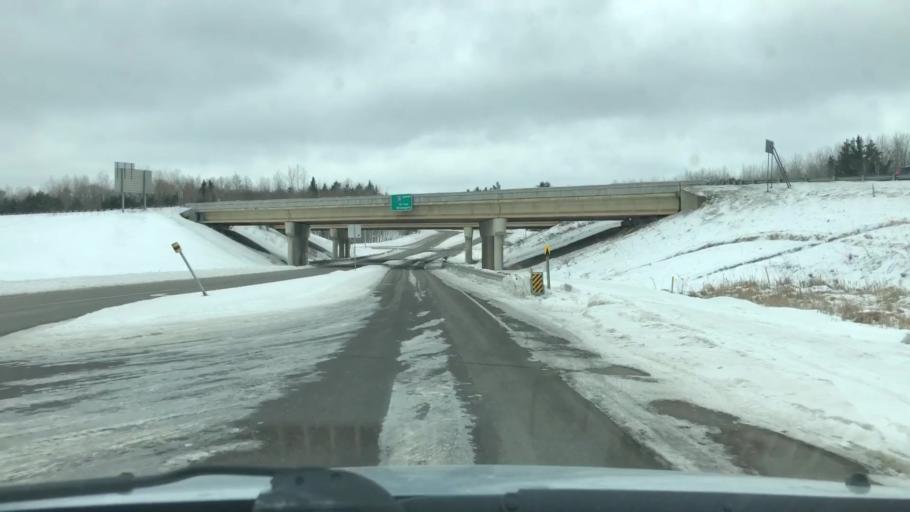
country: US
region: Minnesota
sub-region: Carlton County
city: Esko
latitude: 46.7027
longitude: -92.3005
